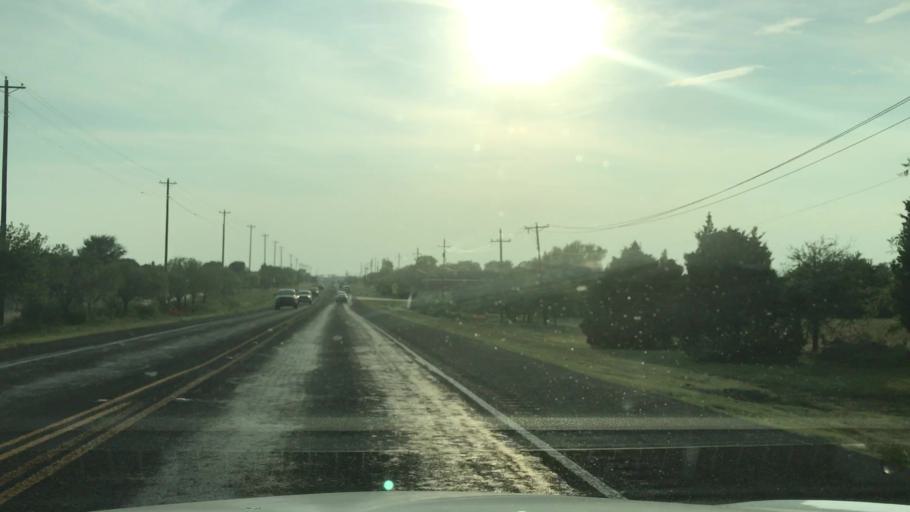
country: US
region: Texas
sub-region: Rockwall County
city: Rockwall
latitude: 32.9067
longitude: -96.4245
